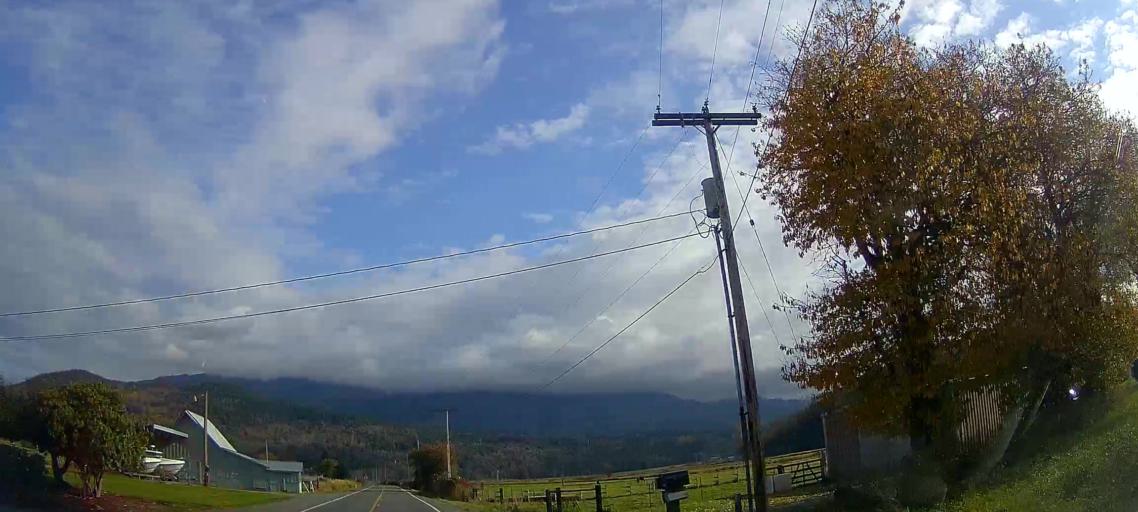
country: US
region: Washington
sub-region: Skagit County
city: Clear Lake
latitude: 48.4525
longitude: -122.2312
